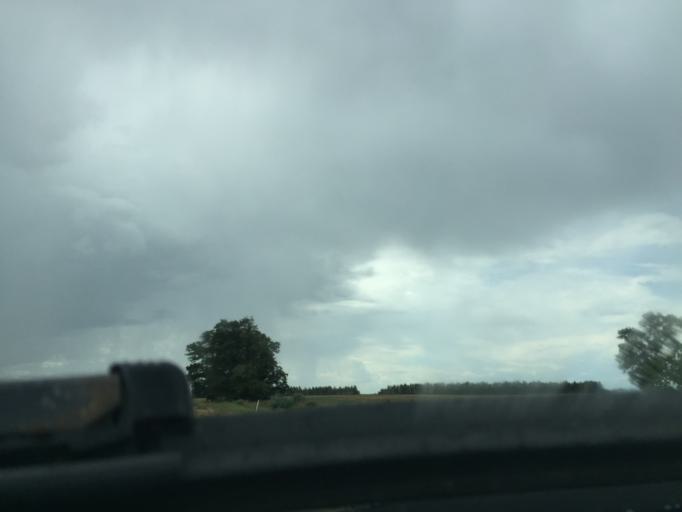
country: LT
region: Siauliu apskritis
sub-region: Joniskis
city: Joniskis
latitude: 56.2922
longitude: 23.7264
